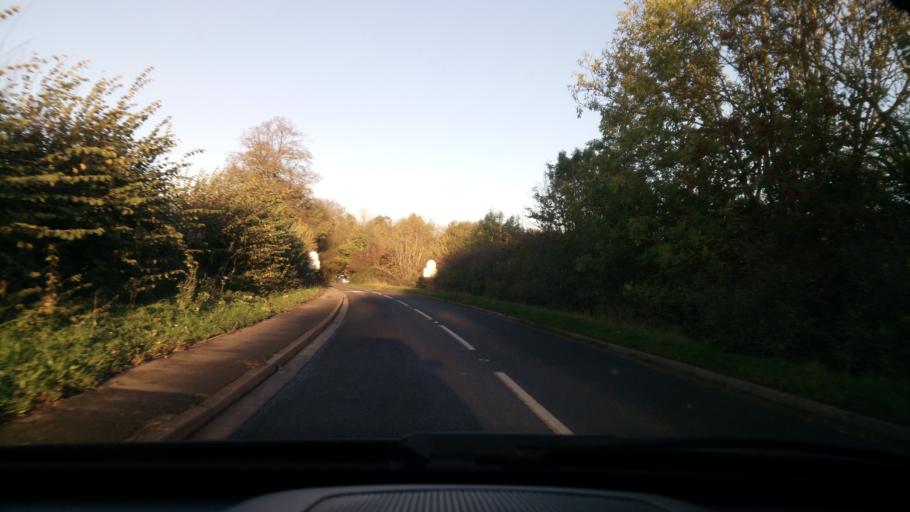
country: GB
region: England
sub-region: Peterborough
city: Ufford
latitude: 52.6382
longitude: -0.3917
